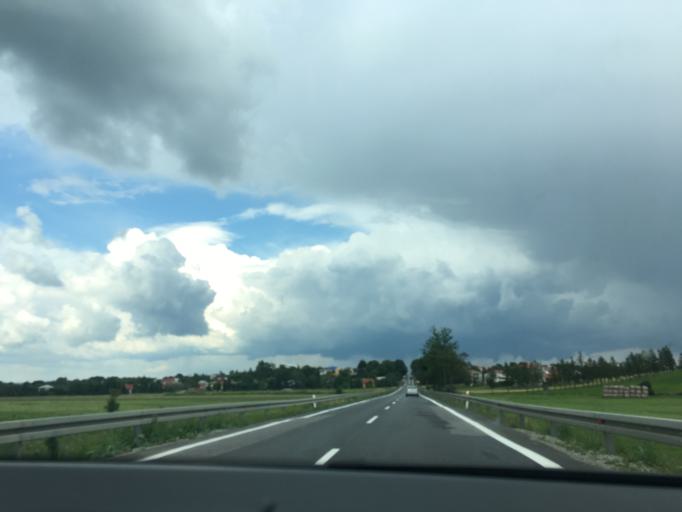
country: PL
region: Subcarpathian Voivodeship
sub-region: Powiat krosnienski
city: Miejsce Piastowe
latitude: 49.6423
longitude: 21.8024
